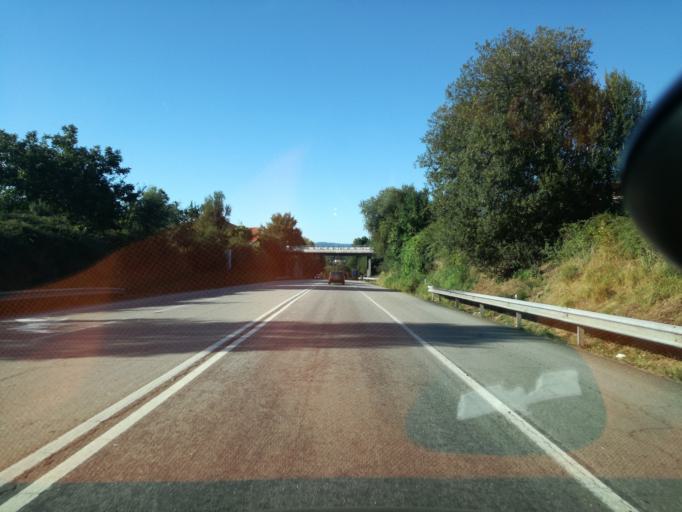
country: PT
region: Porto
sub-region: Santo Tirso
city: Sao Miguel do Couto
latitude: 41.3191
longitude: -8.4692
